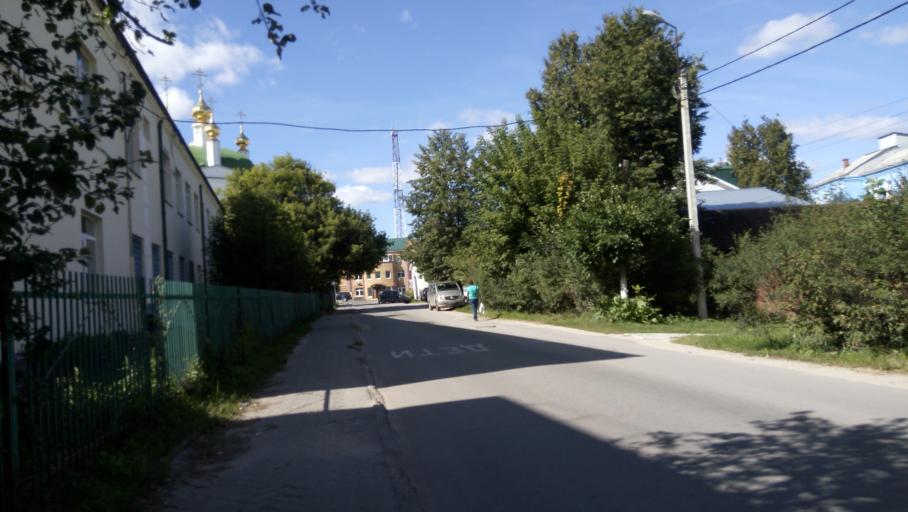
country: RU
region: Nizjnij Novgorod
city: Bor
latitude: 56.3599
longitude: 44.0582
